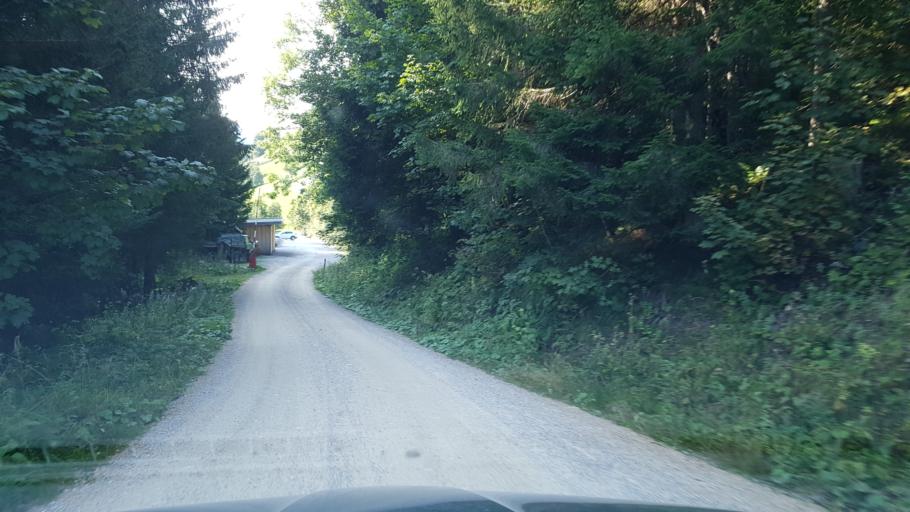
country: AT
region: Salzburg
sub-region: Politischer Bezirk Sankt Johann im Pongau
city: Kleinarl
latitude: 47.2740
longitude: 13.2463
